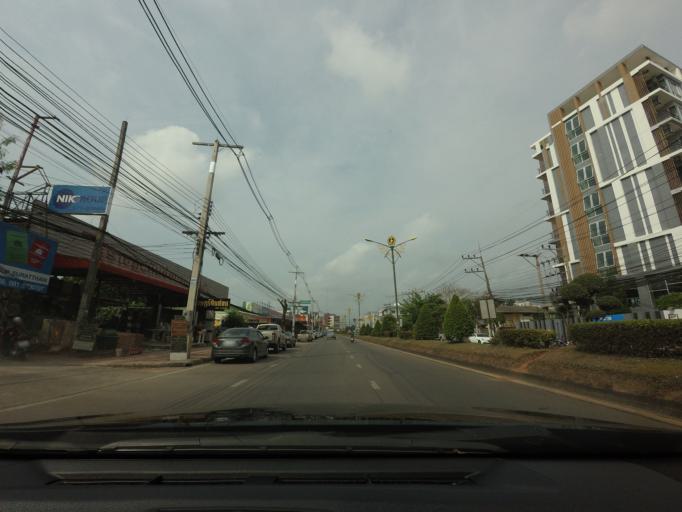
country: TH
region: Surat Thani
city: Surat Thani
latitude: 9.1262
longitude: 99.3127
